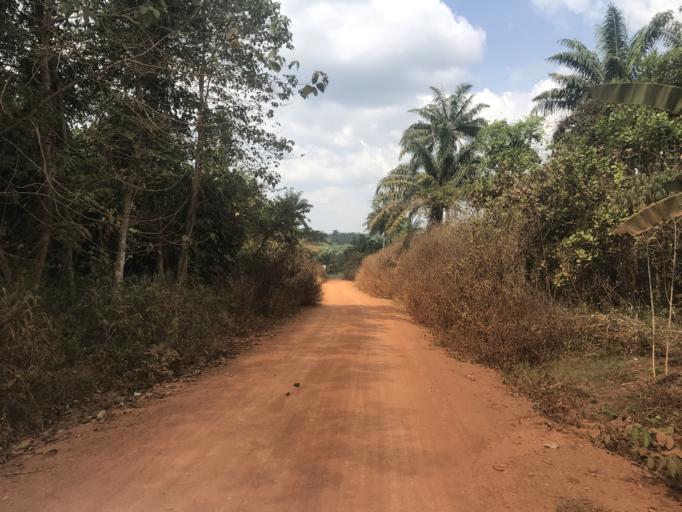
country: NG
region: Osun
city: Inisa
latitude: 7.8731
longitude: 4.3835
